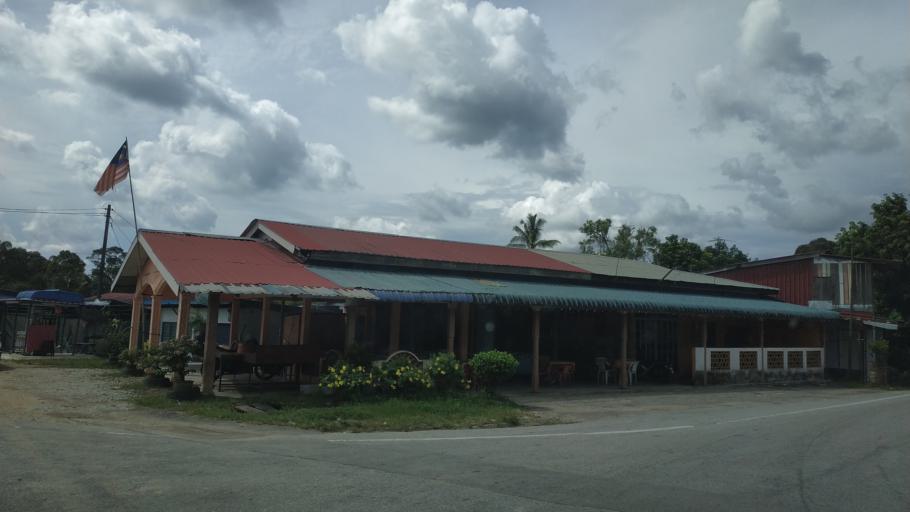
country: MY
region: Kedah
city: Kulim
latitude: 5.4286
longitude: 100.6598
